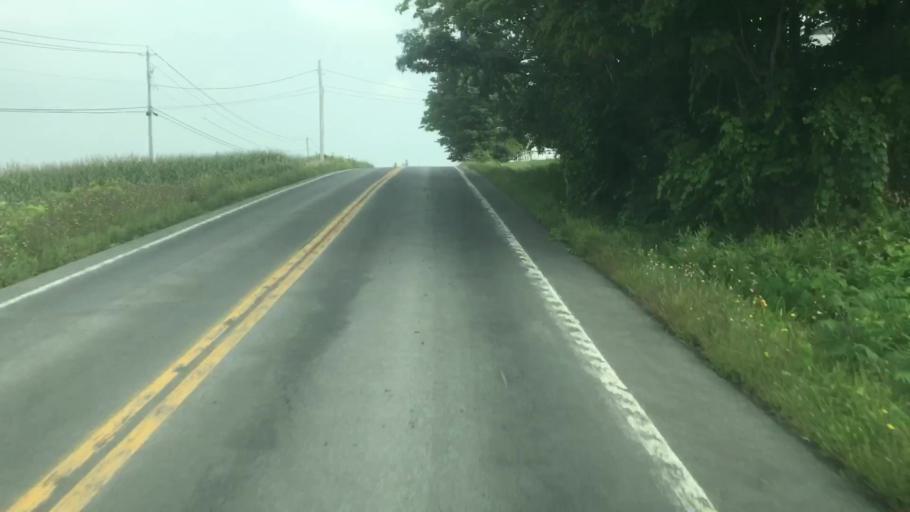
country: US
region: New York
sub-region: Onondaga County
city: Skaneateles
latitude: 42.8908
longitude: -76.4501
